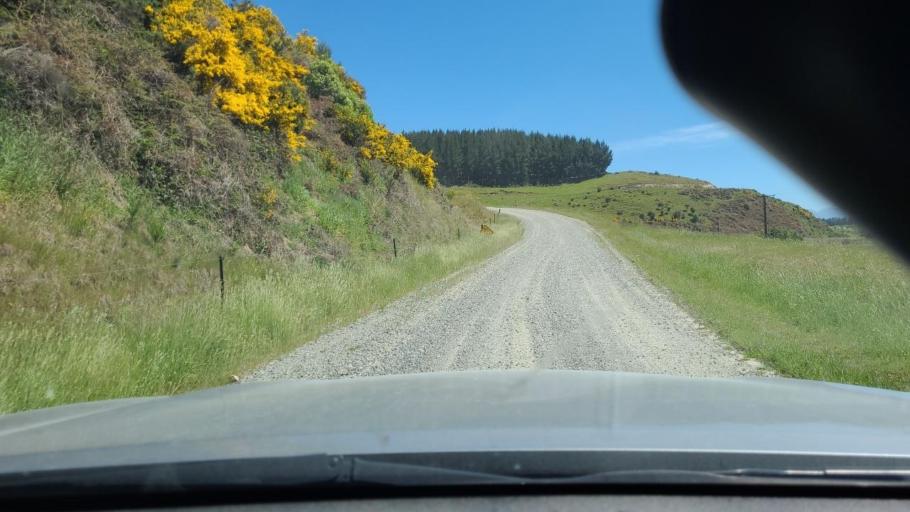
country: NZ
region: Southland
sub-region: Southland District
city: Te Anau
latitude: -45.6181
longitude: 167.6885
